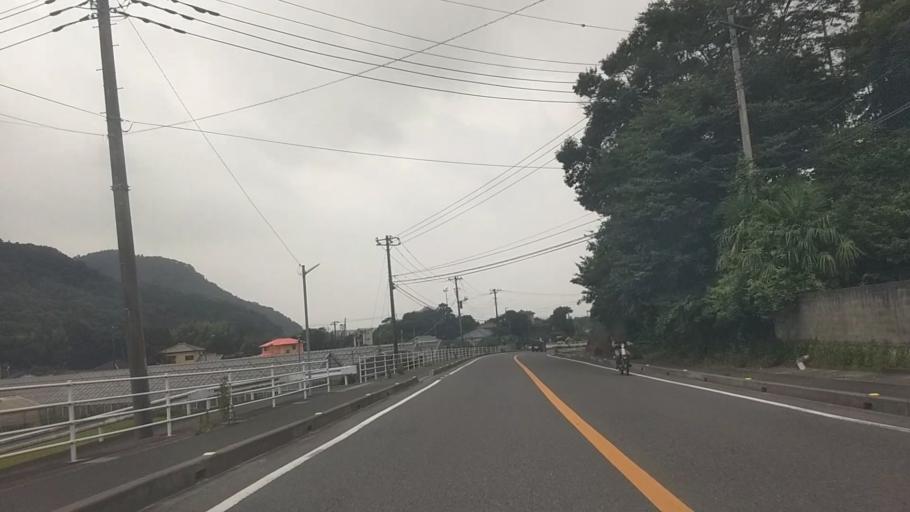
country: JP
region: Chiba
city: Tateyama
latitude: 35.1449
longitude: 139.8566
